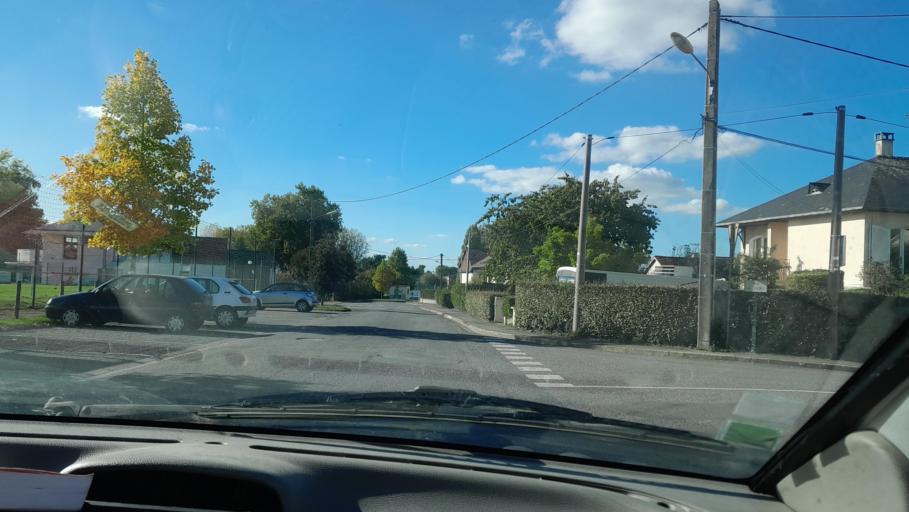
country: FR
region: Pays de la Loire
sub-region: Departement de la Mayenne
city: Quelaines-Saint-Gault
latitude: 47.9236
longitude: -0.8049
